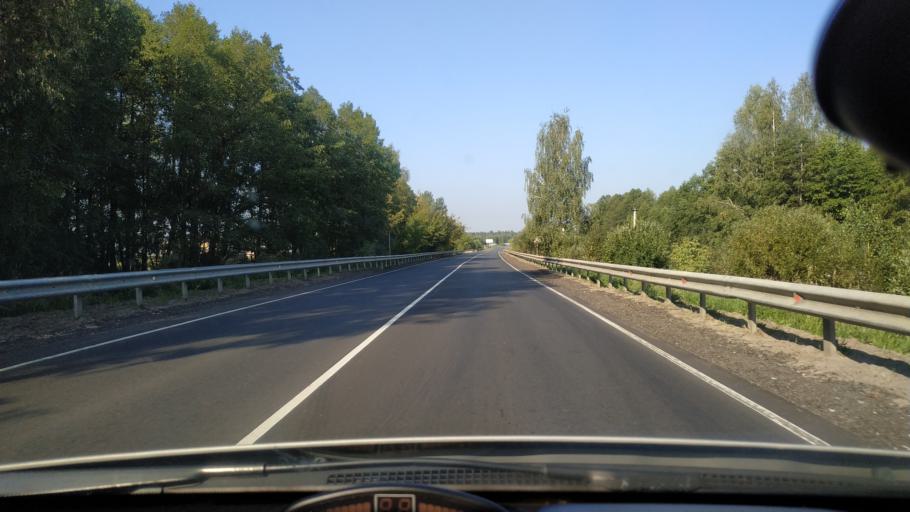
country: RU
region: Moskovskaya
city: Misheronskiy
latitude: 55.6582
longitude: 39.7618
